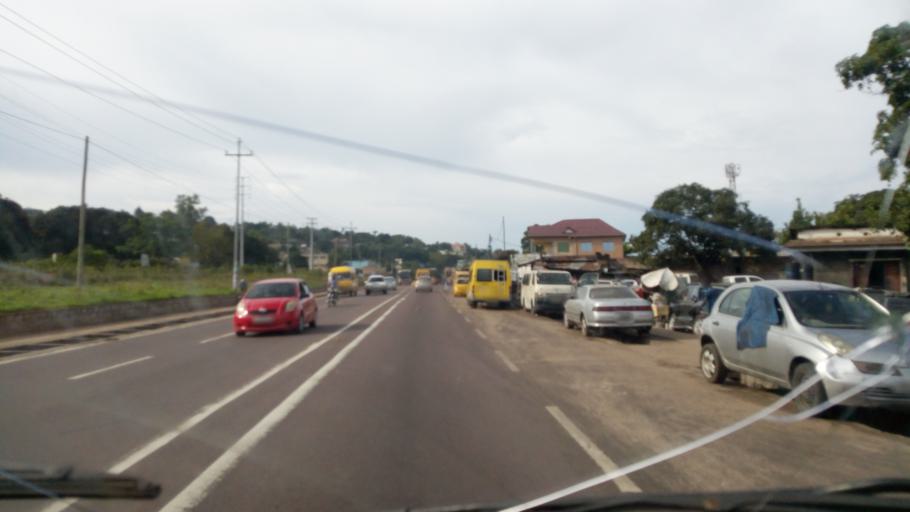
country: CD
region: Kinshasa
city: Kinshasa
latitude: -4.4273
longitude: 15.2578
